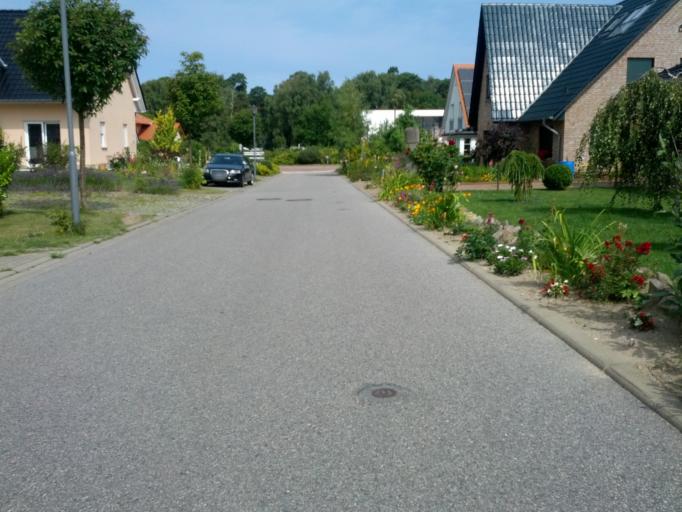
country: DE
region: Mecklenburg-Vorpommern
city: Bastorf
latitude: 54.1499
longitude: 11.7134
